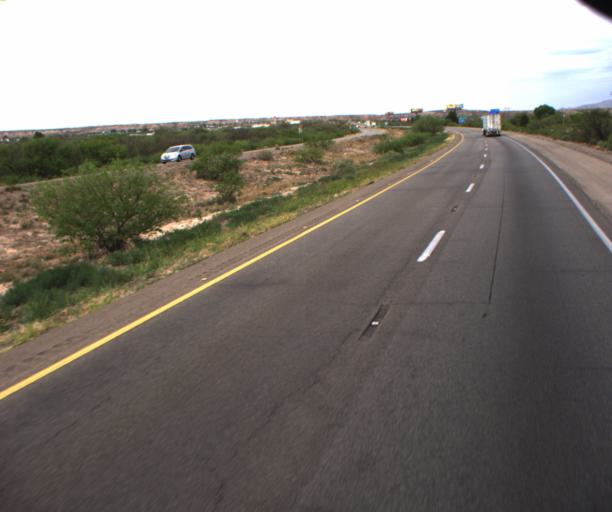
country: US
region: Arizona
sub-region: Cochise County
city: Benson
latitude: 31.9780
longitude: -110.2938
